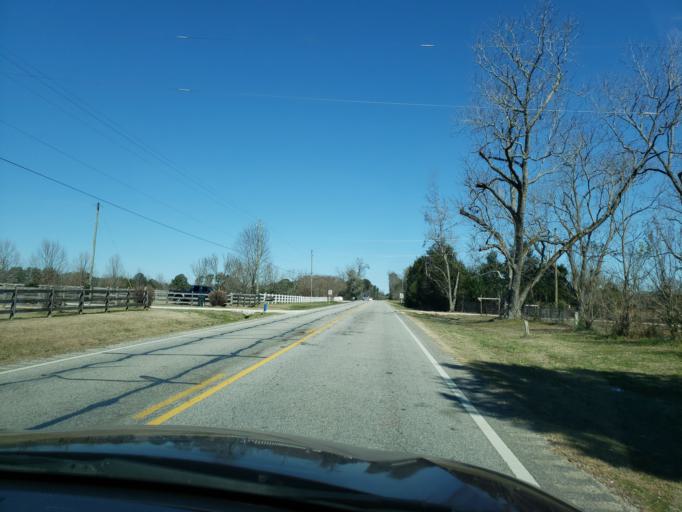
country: US
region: Alabama
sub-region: Macon County
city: Tuskegee
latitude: 32.5787
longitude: -85.6548
